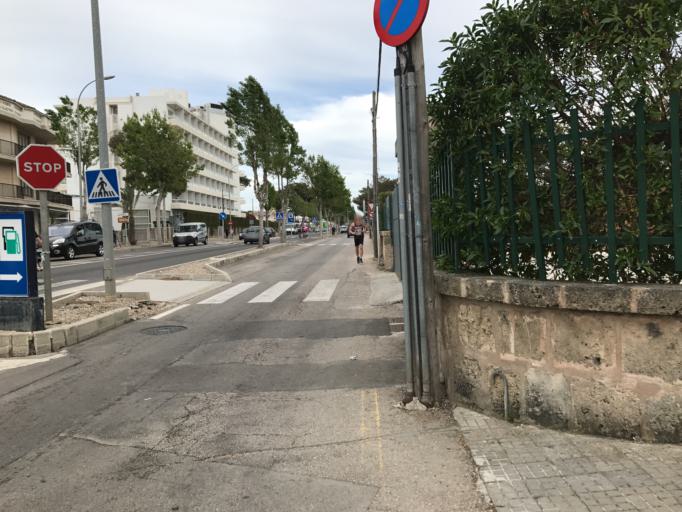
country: ES
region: Balearic Islands
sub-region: Illes Balears
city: Santa Margalida
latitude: 39.7641
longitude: 3.1498
